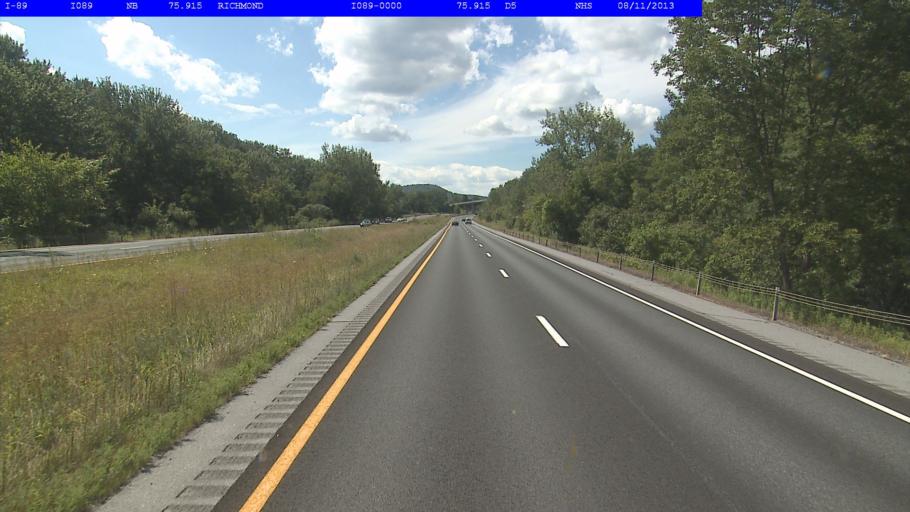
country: US
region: Vermont
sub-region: Chittenden County
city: Williston
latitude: 44.3989
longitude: -72.9787
